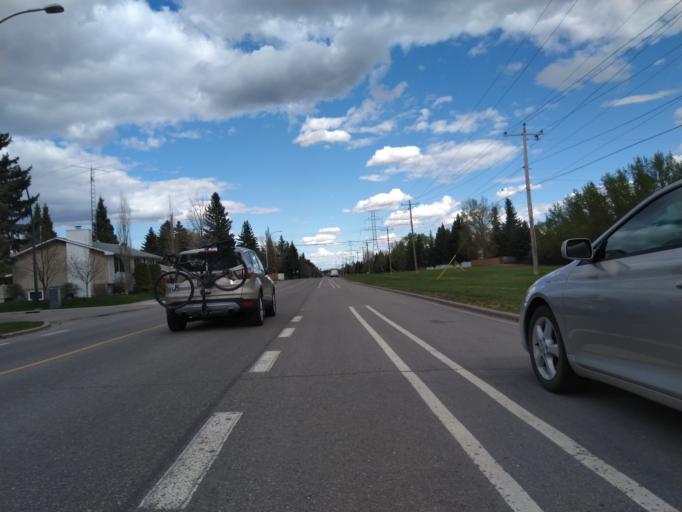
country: CA
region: Alberta
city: Calgary
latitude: 50.9945
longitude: -114.1374
